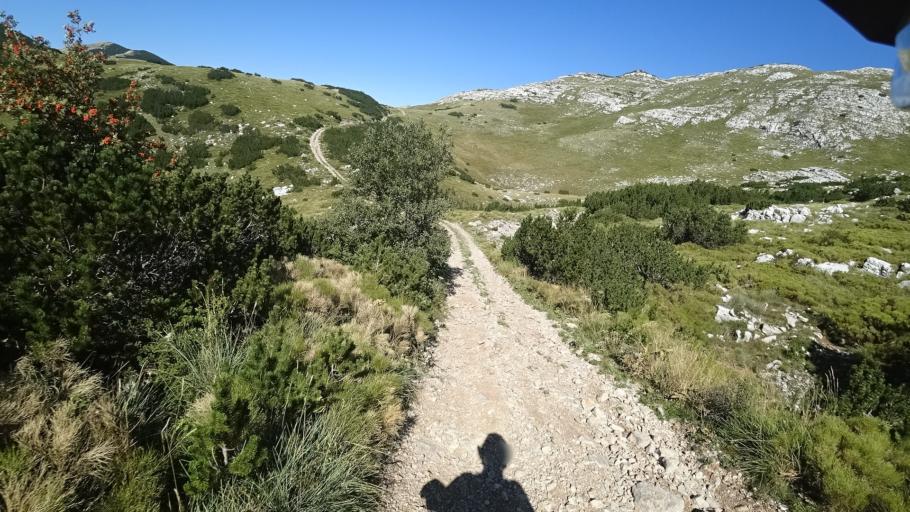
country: HR
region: Splitsko-Dalmatinska
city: Hrvace
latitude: 43.9383
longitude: 16.5887
